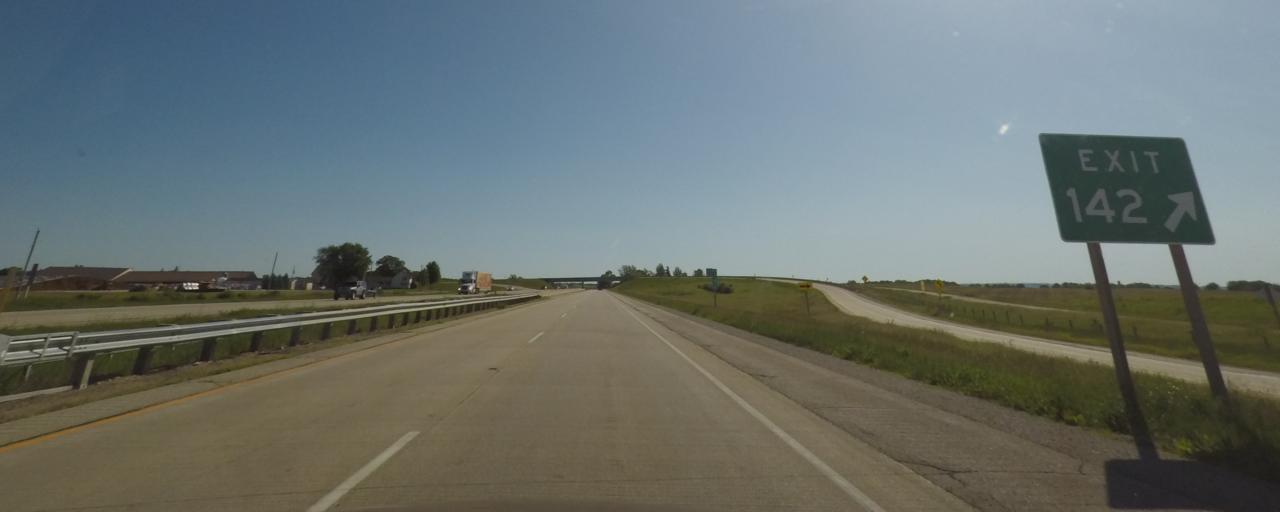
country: US
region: Wisconsin
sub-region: Fond du Lac County
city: Waupun
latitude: 43.5812
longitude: -88.7559
